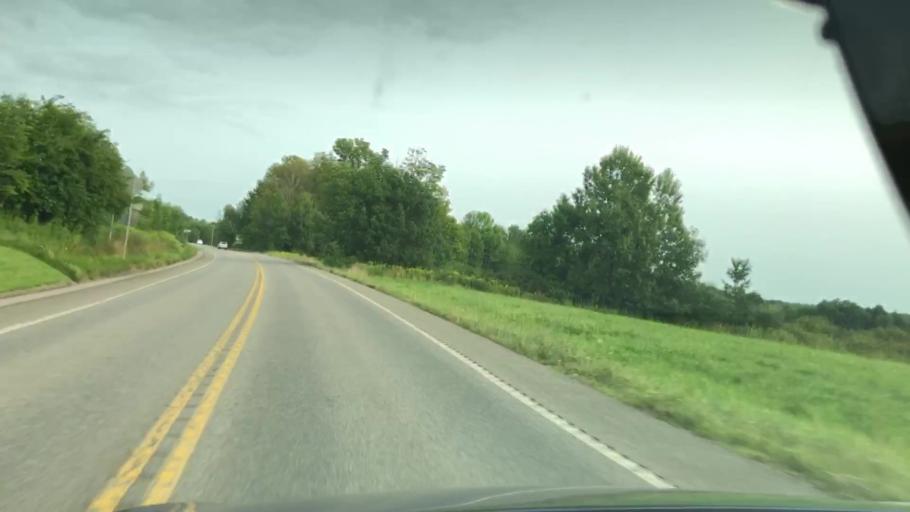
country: US
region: Pennsylvania
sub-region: Erie County
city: Union City
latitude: 41.8320
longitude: -79.8168
